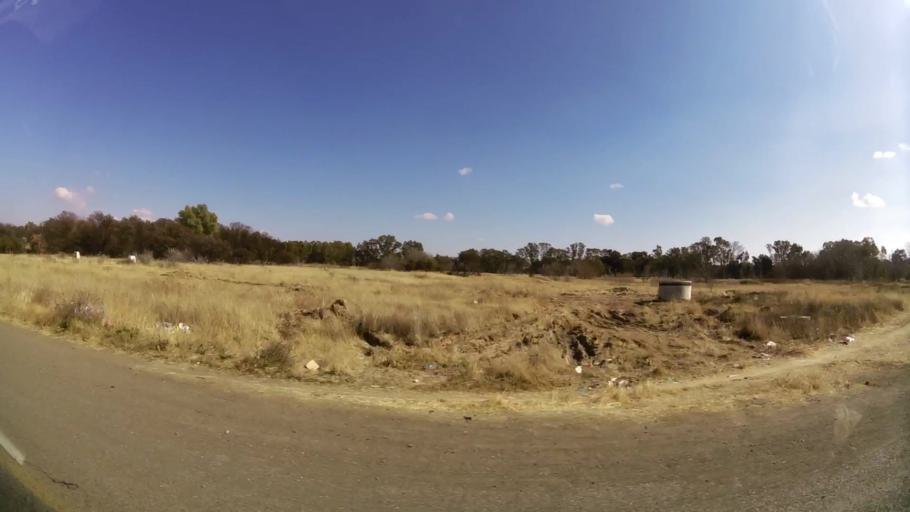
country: ZA
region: Orange Free State
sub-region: Mangaung Metropolitan Municipality
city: Bloemfontein
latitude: -29.1202
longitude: 26.2670
